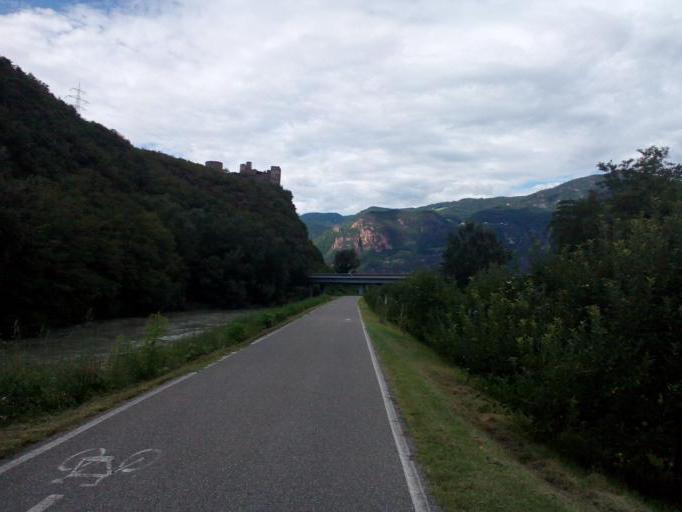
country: IT
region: Trentino-Alto Adige
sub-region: Bolzano
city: Cornaiano
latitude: 46.4759
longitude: 11.3089
